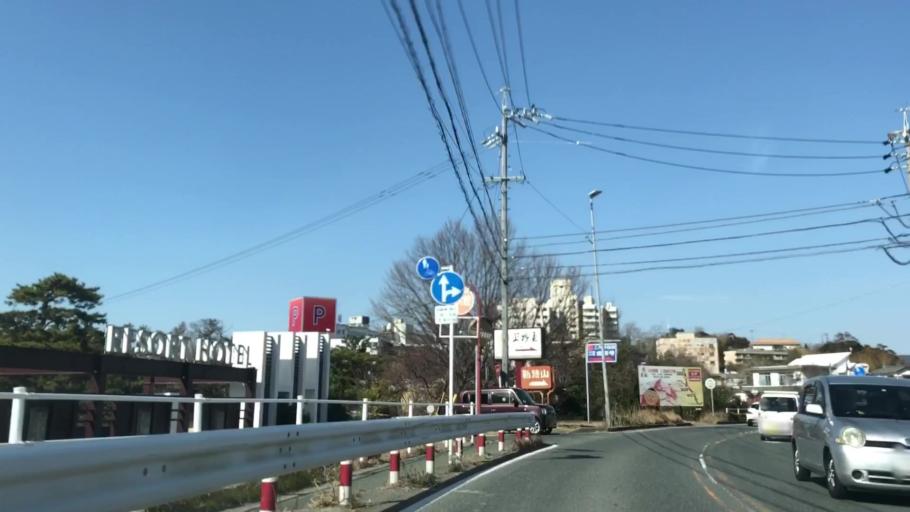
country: JP
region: Aichi
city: Gamagori
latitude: 34.8056
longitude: 137.2601
